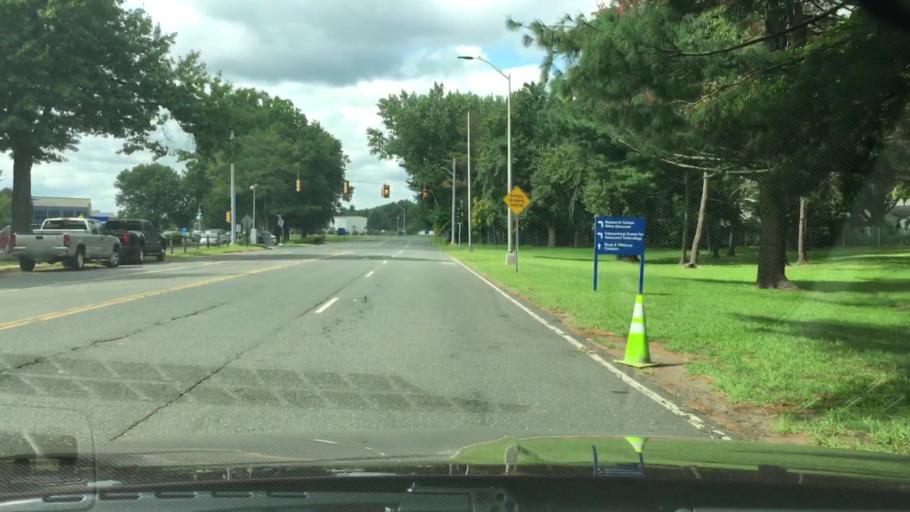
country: US
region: Connecticut
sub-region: Hartford County
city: East Hartford
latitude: 41.7607
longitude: -72.6274
